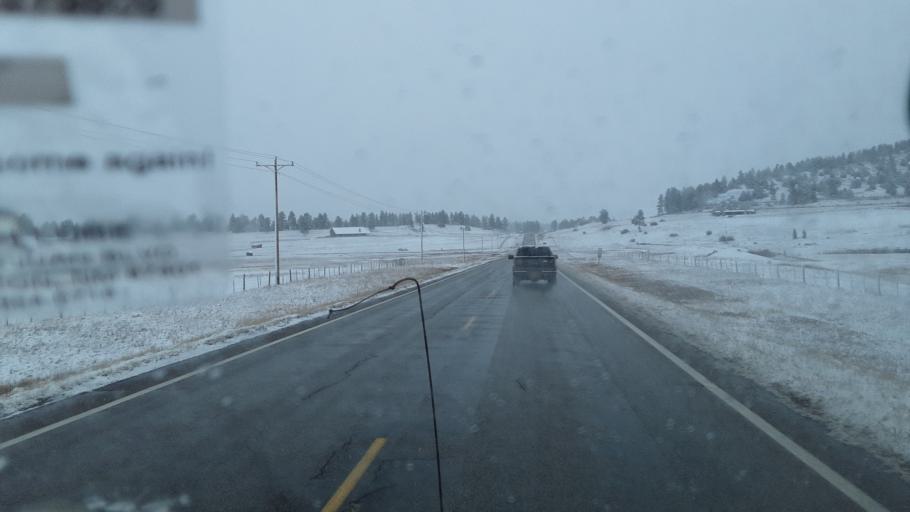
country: US
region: Colorado
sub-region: Archuleta County
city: Pagosa Springs
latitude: 37.2148
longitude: -106.9834
